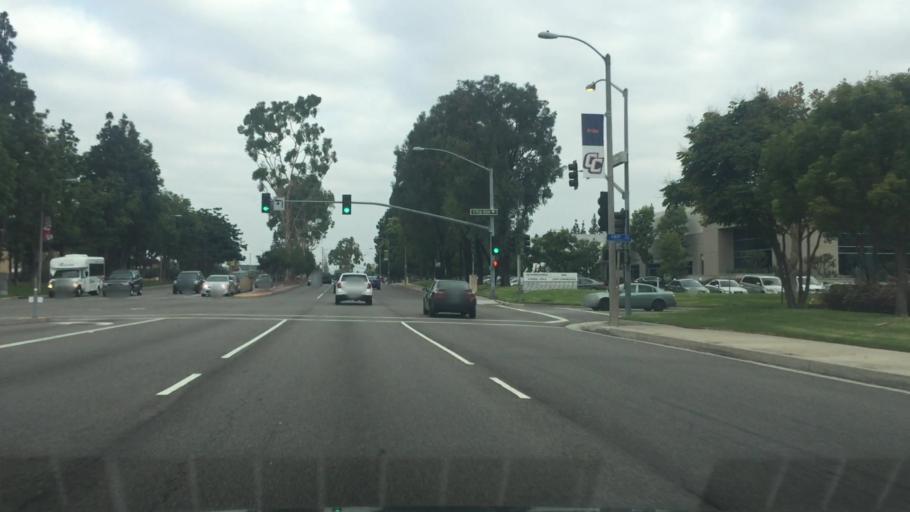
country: US
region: California
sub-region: Orange County
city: Cypress
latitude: 33.8053
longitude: -118.0282
